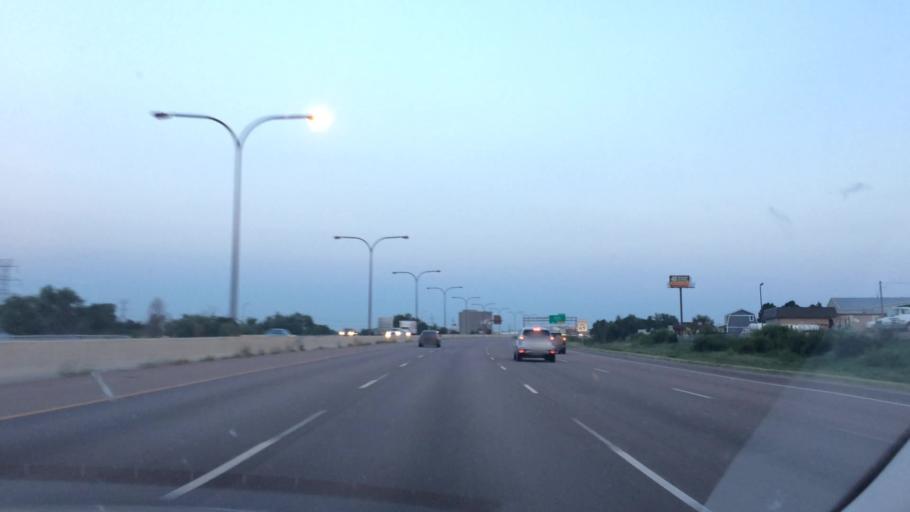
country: US
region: Colorado
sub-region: El Paso County
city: Colorado Springs
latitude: 38.8072
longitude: -104.8051
